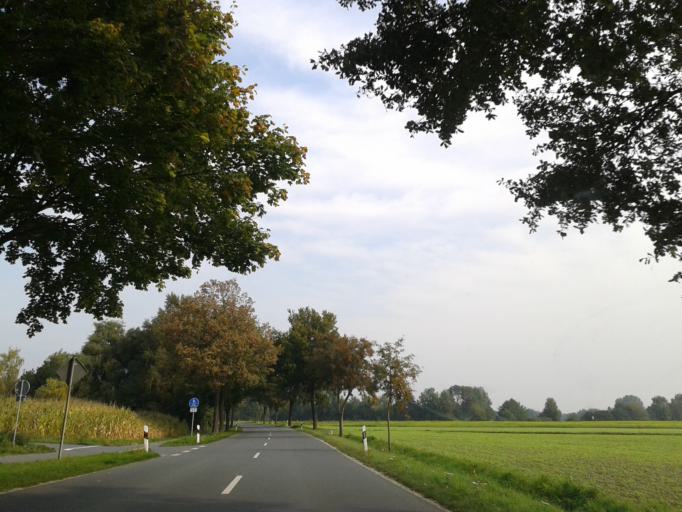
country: DE
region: North Rhine-Westphalia
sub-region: Regierungsbezirk Detmold
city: Delbruck
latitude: 51.7412
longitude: 8.6288
